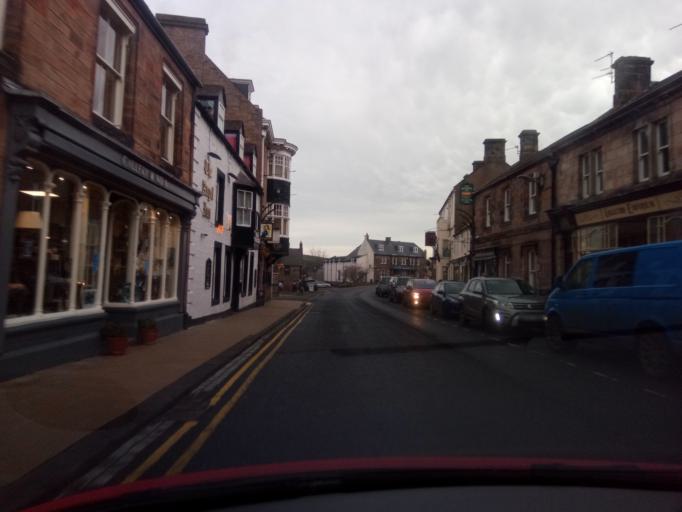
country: GB
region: England
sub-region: Northumberland
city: Wooler
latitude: 55.5464
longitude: -2.0157
